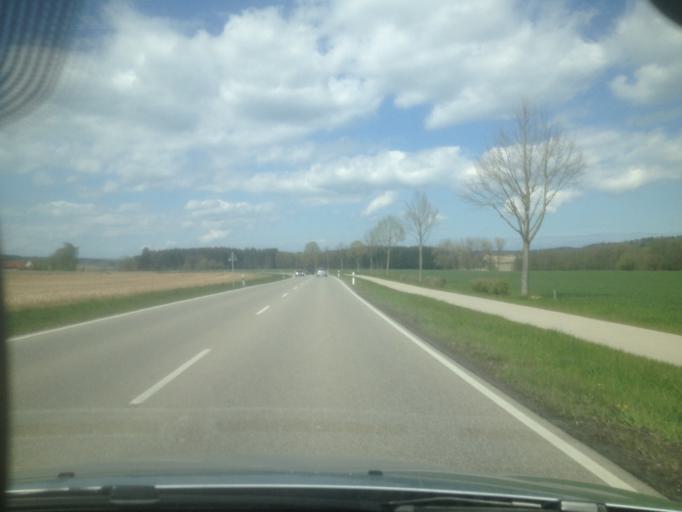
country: DE
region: Bavaria
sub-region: Swabia
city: Adelsried
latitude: 48.3889
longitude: 10.7219
